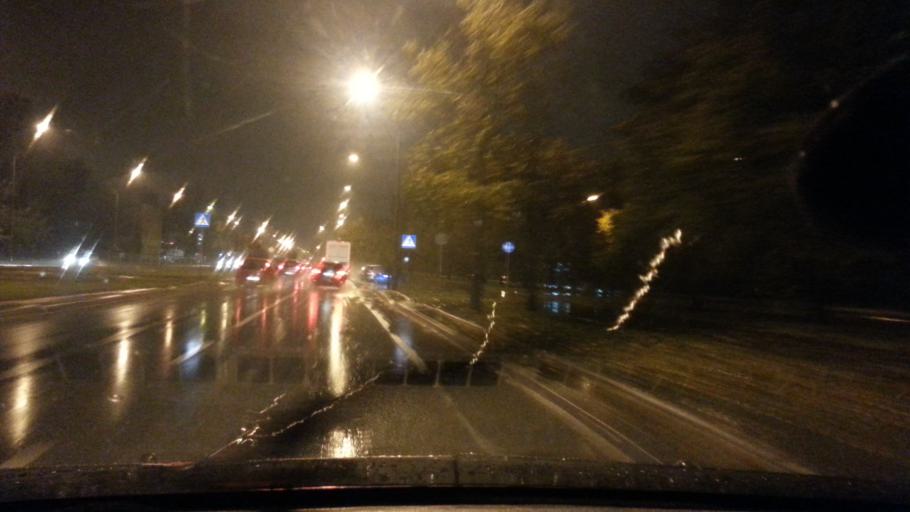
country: PL
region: Masovian Voivodeship
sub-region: Warszawa
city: Targowek
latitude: 52.2822
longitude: 21.0251
